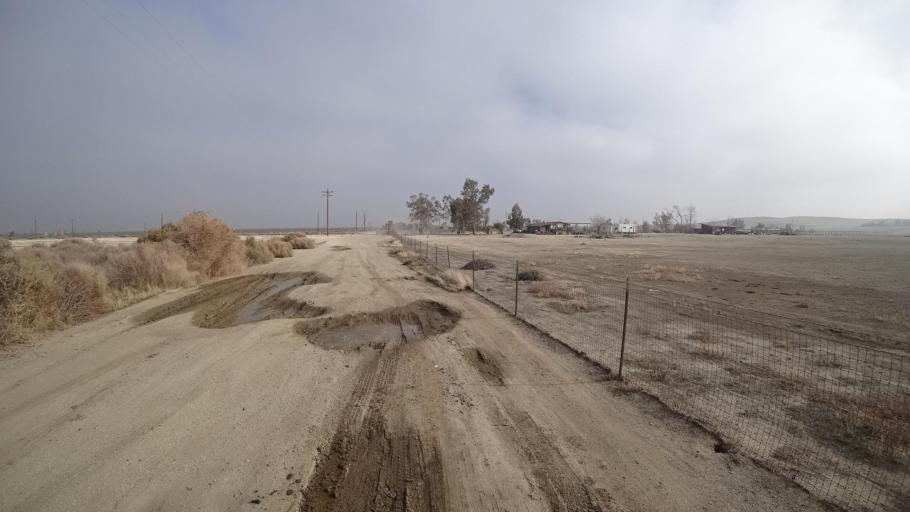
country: US
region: California
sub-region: Kern County
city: Maricopa
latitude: 35.0471
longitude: -119.3599
